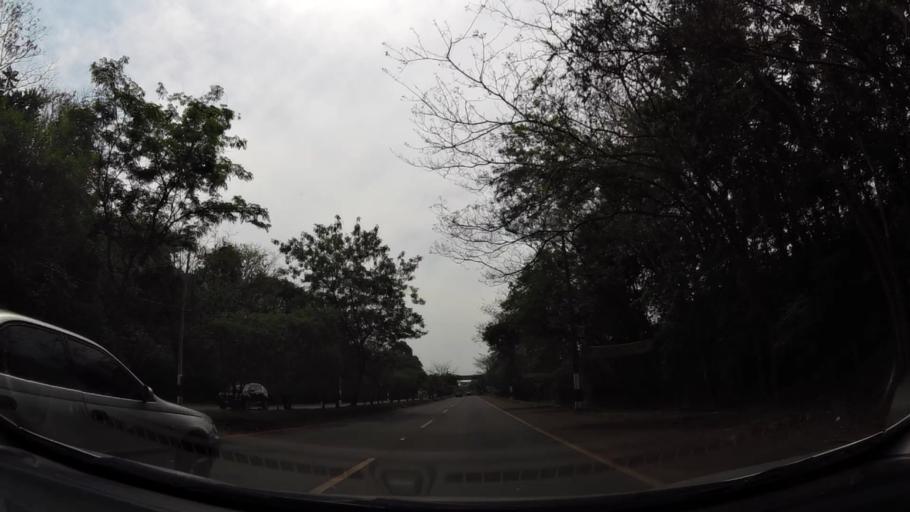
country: PY
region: Alto Parana
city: Ciudad del Este
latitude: -25.4878
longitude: -54.6293
